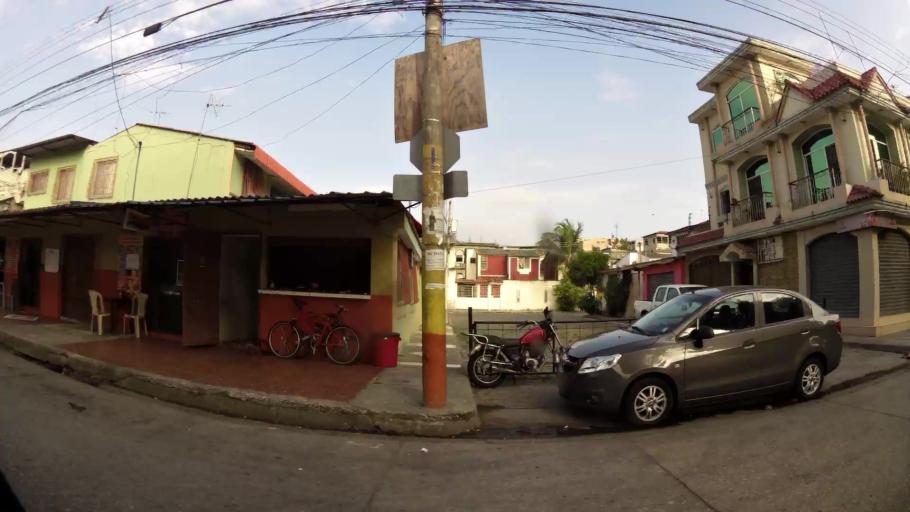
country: EC
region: Guayas
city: Eloy Alfaro
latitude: -2.1292
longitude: -79.8960
